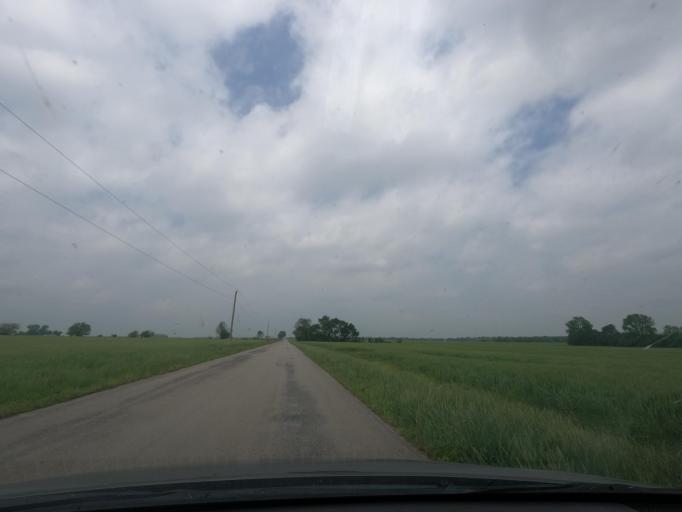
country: US
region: Kansas
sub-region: Cherokee County
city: Columbus
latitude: 37.2758
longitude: -94.9406
